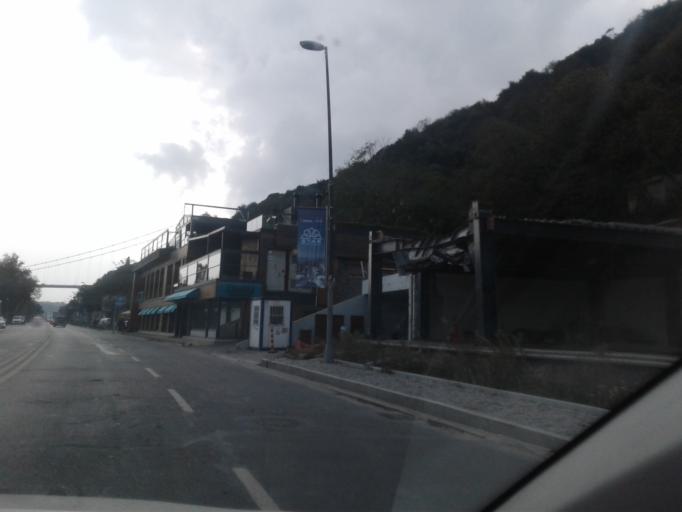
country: TR
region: Istanbul
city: UEskuedar
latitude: 41.0566
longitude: 29.0346
